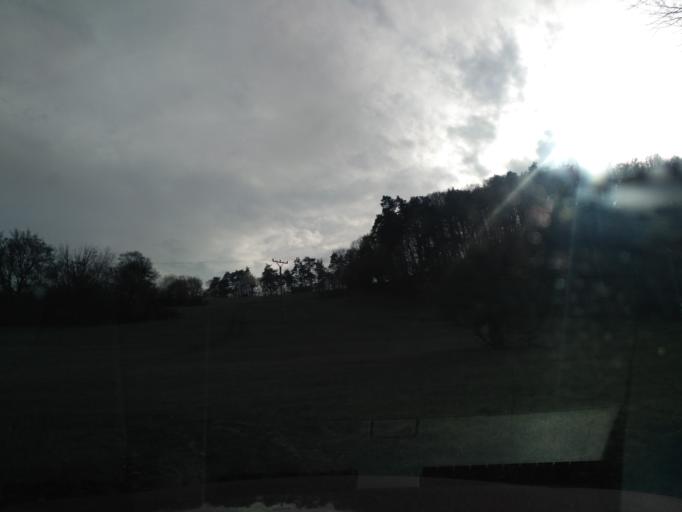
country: SK
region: Presovsky
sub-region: Okres Presov
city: Presov
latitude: 48.8740
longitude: 21.2284
